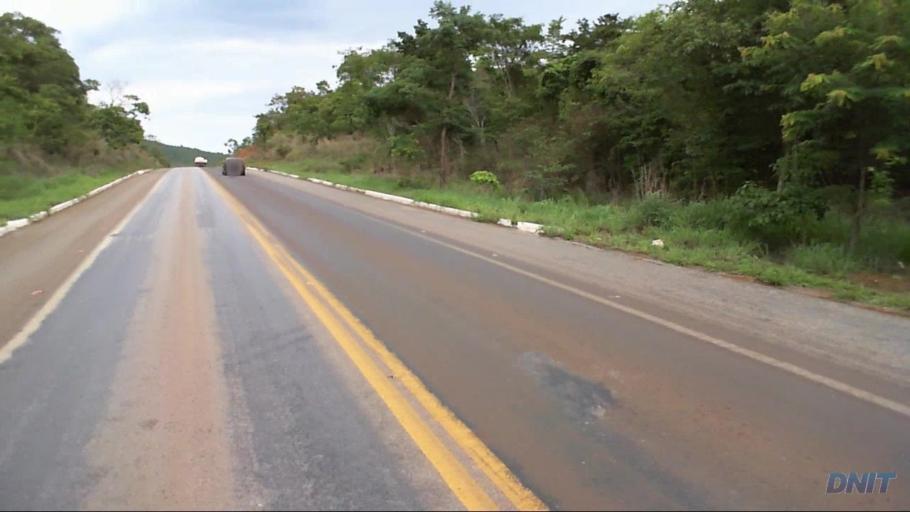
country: BR
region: Goias
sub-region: Barro Alto
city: Barro Alto
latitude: -14.9383
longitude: -48.9419
